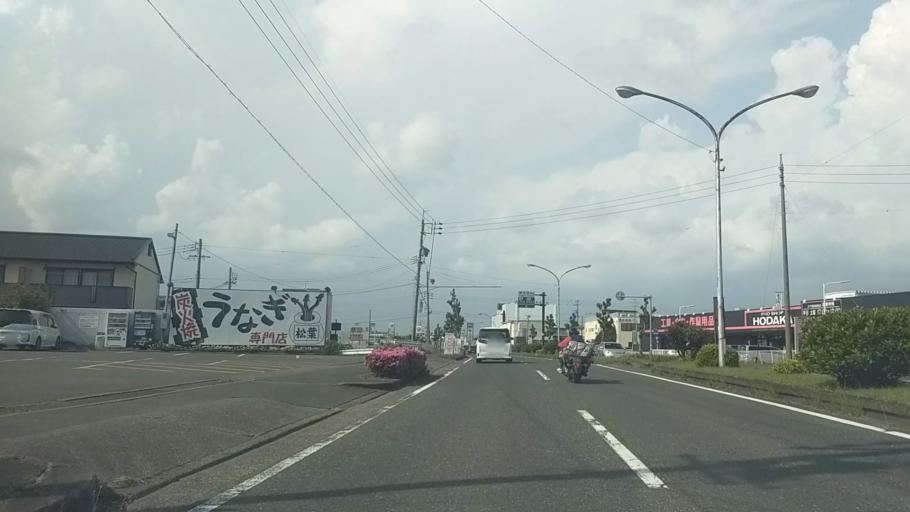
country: JP
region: Shizuoka
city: Hamakita
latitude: 34.7382
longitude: 137.7897
